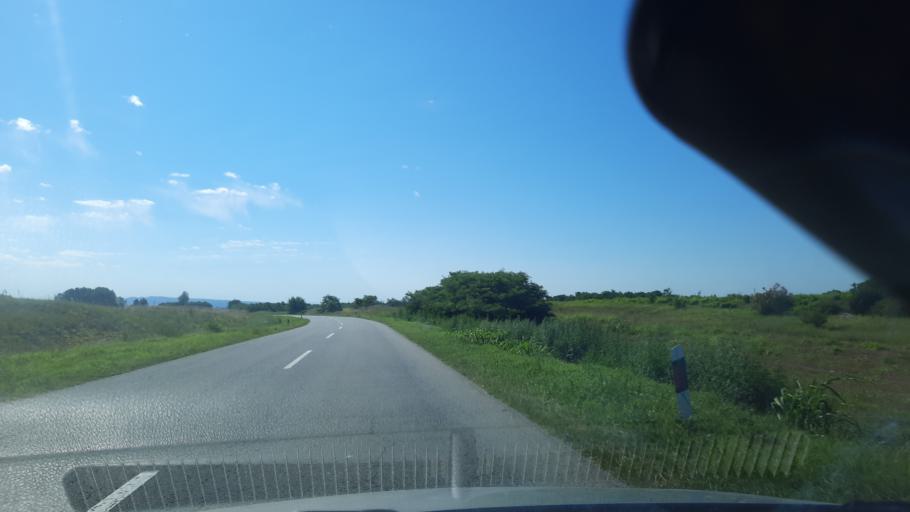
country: RS
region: Central Serbia
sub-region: Branicevski Okrug
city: Pozarevac
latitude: 44.8046
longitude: 21.1770
